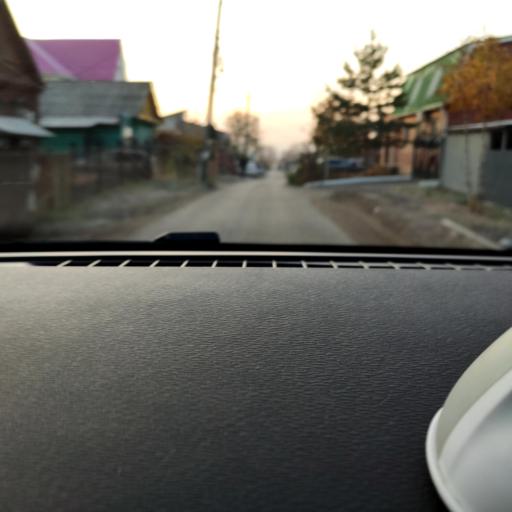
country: RU
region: Samara
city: Samara
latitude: 53.1851
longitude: 50.1852
